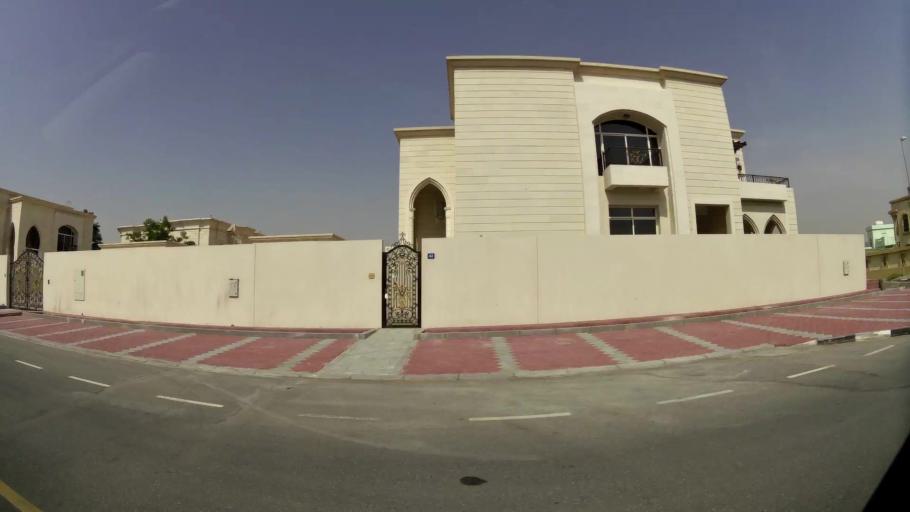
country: AE
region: Ash Shariqah
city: Sharjah
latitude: 25.2493
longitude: 55.4319
